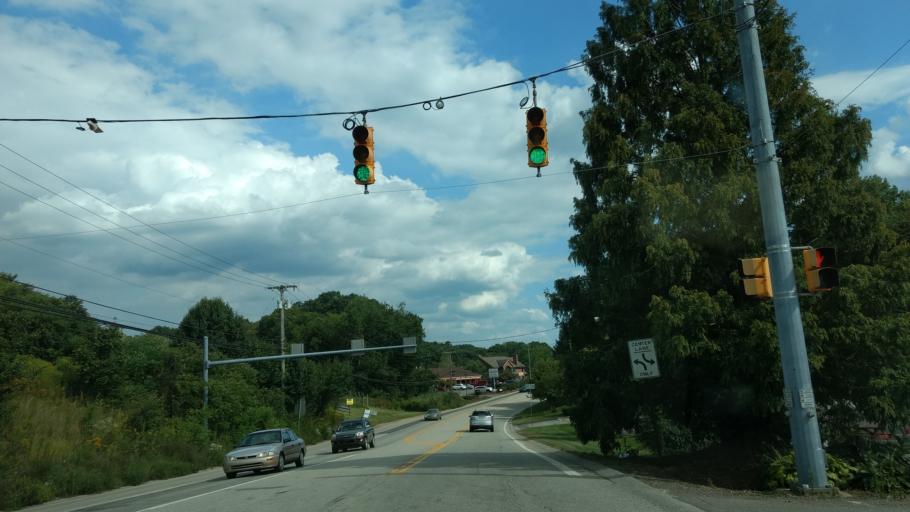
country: US
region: Pennsylvania
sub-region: Allegheny County
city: Bradford Woods
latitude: 40.6144
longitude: -80.0917
